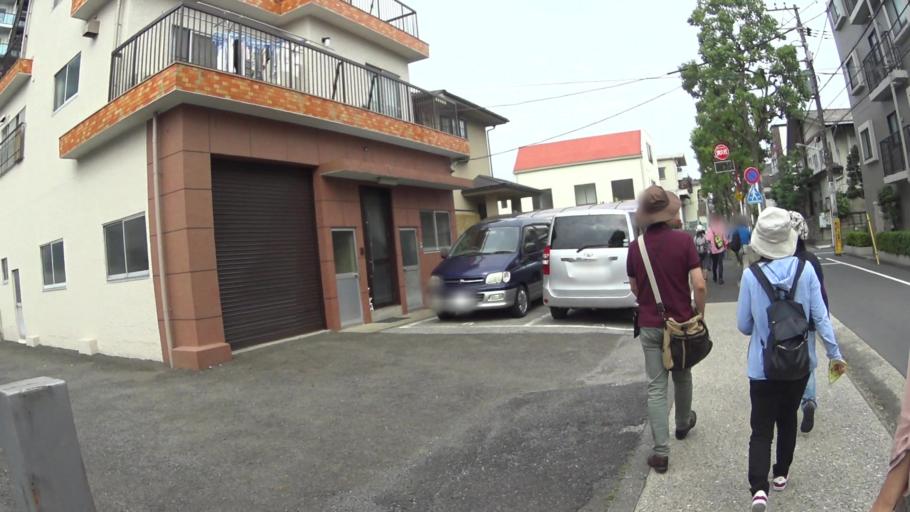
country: JP
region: Tokyo
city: Urayasu
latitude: 35.7062
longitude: 139.8487
